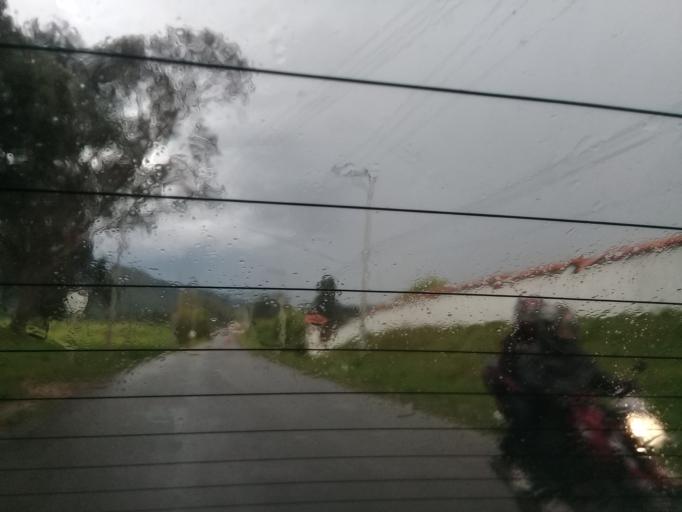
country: CO
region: Cundinamarca
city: Zipaquira
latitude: 5.0018
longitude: -73.9763
